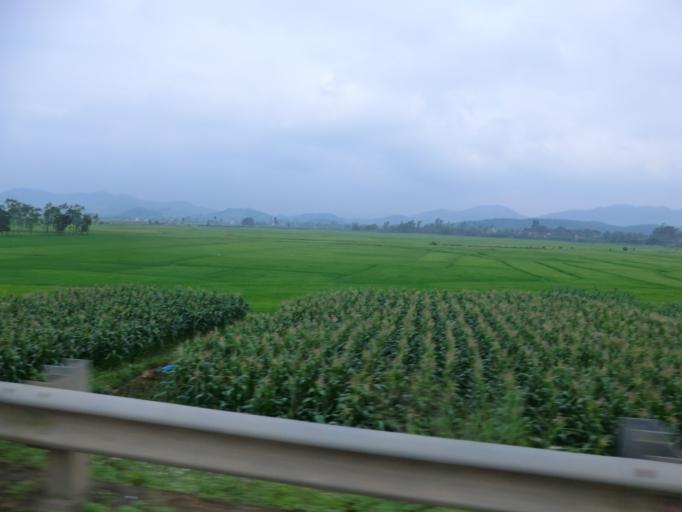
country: VN
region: Quang Binh
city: Ba Don
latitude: 17.6082
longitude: 106.3438
